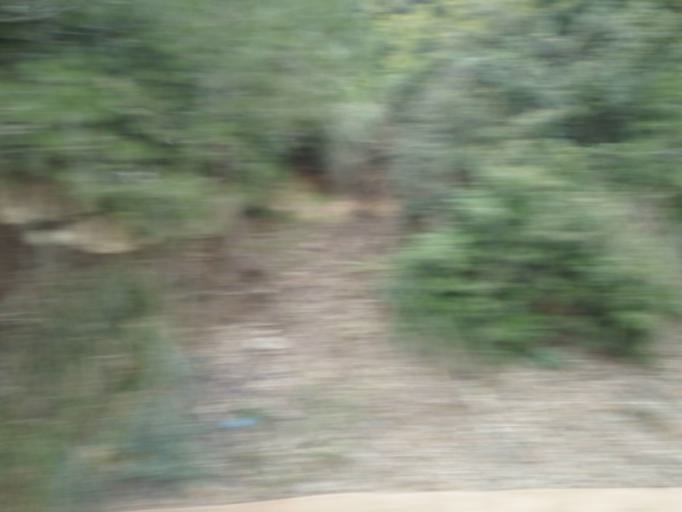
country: DZ
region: Tipaza
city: Tipasa
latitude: 36.5856
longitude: 2.5444
